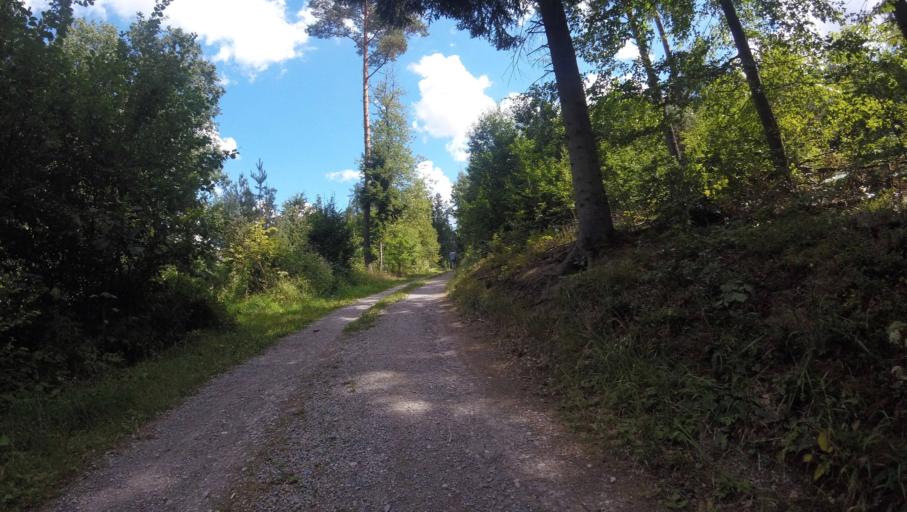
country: DE
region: Baden-Wuerttemberg
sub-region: Regierungsbezirk Stuttgart
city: Oppenweiler
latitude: 48.9895
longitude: 9.4333
